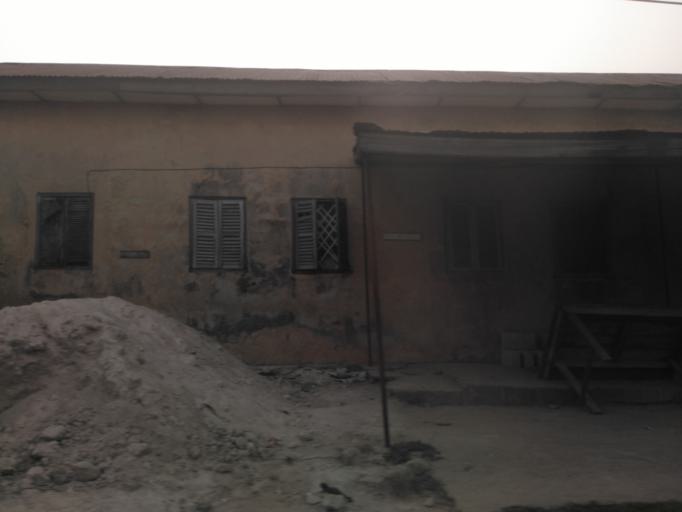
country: GH
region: Ashanti
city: Tafo
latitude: 6.7103
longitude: -1.6051
